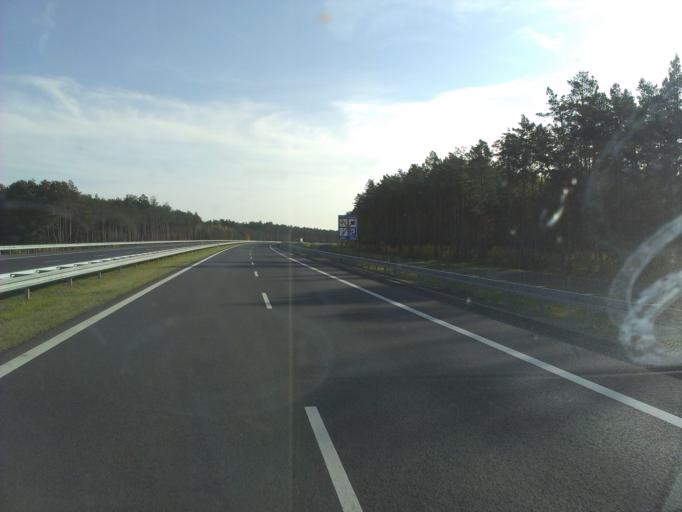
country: PL
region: Lubusz
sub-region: Powiat gorzowski
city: Deszczno
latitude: 52.6416
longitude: 15.3600
